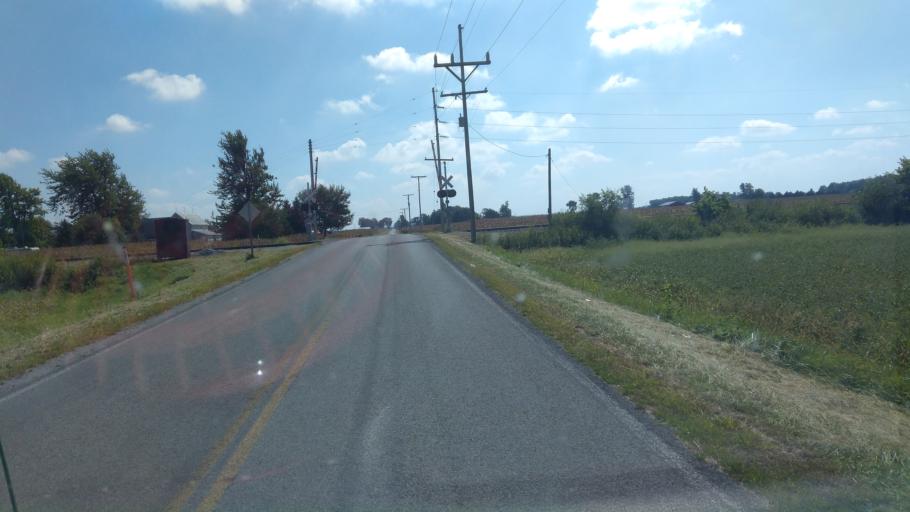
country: US
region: Ohio
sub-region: Hardin County
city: Ada
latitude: 40.7751
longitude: -83.7849
